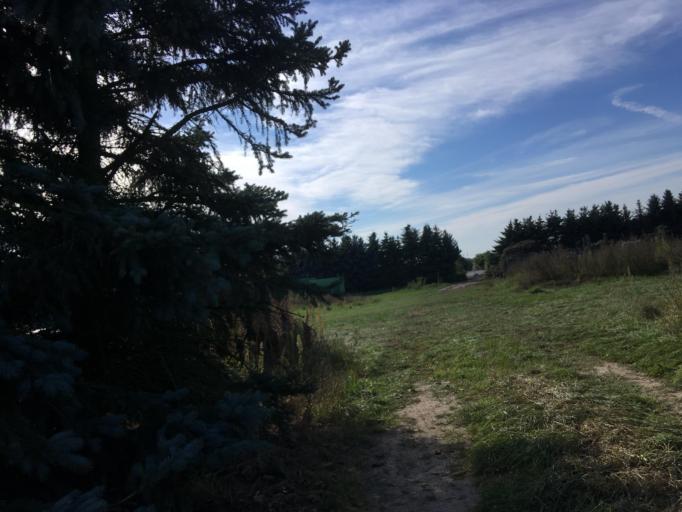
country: DE
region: Berlin
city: Falkenberg
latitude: 52.6068
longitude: 13.5465
